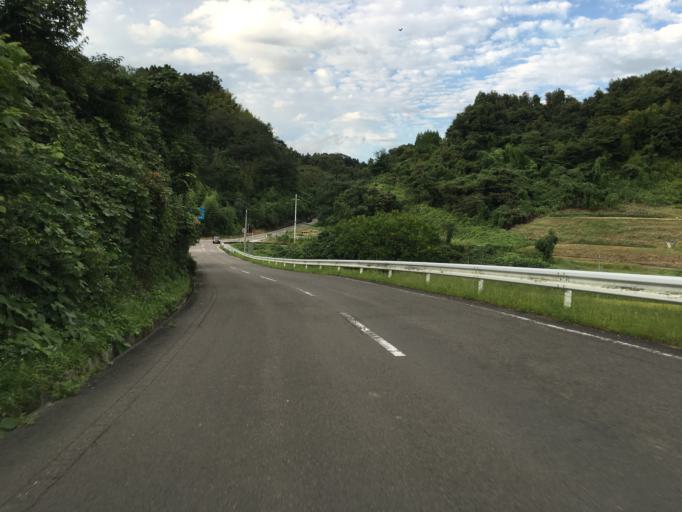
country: JP
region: Fukushima
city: Nihommatsu
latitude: 37.5974
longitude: 140.4973
